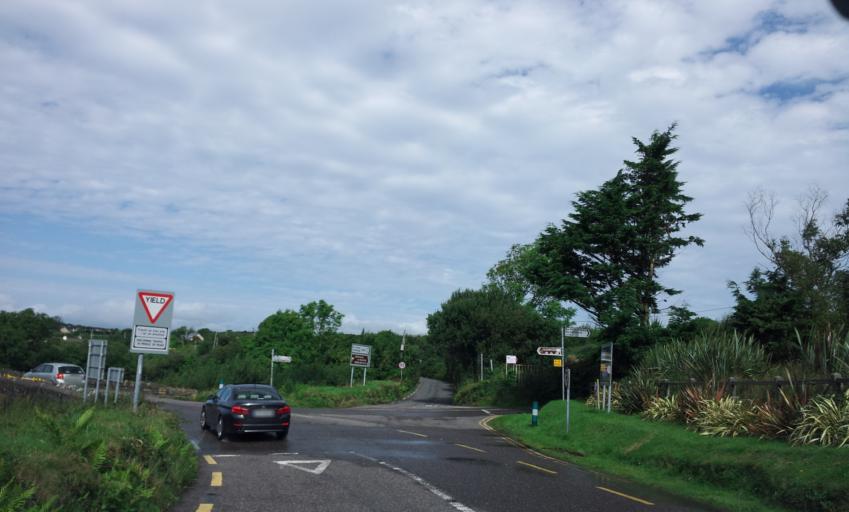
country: IE
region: Munster
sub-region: Ciarrai
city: Killorglin
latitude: 52.0682
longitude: -9.9028
